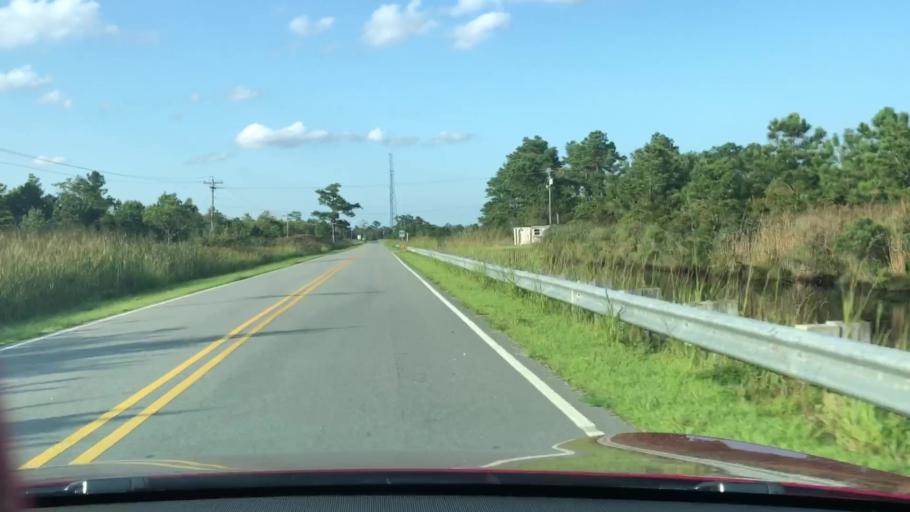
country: US
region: North Carolina
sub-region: Dare County
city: Wanchese
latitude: 35.6997
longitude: -75.7719
